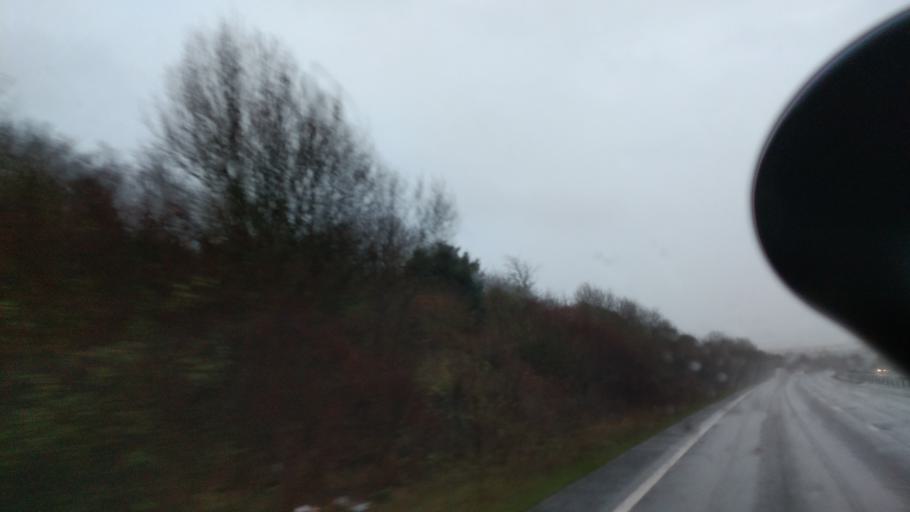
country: GB
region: England
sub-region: East Sussex
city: Portslade
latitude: 50.8506
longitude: -0.2426
